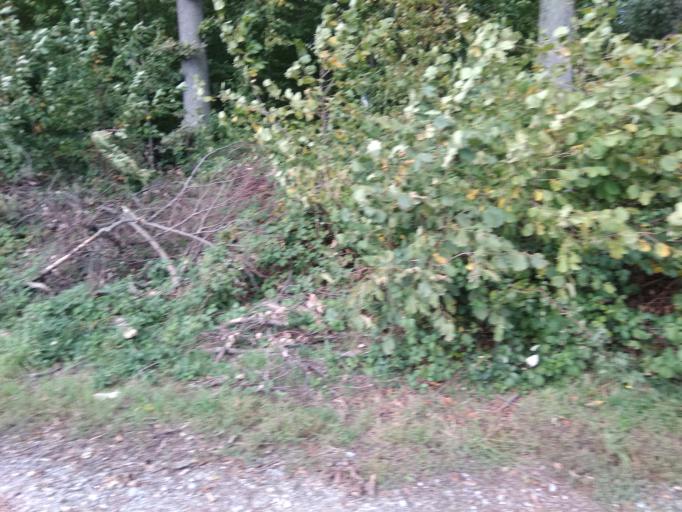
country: DE
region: Baden-Wuerttemberg
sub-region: Regierungsbezirk Stuttgart
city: Eberstadt
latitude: 49.1688
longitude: 9.3357
